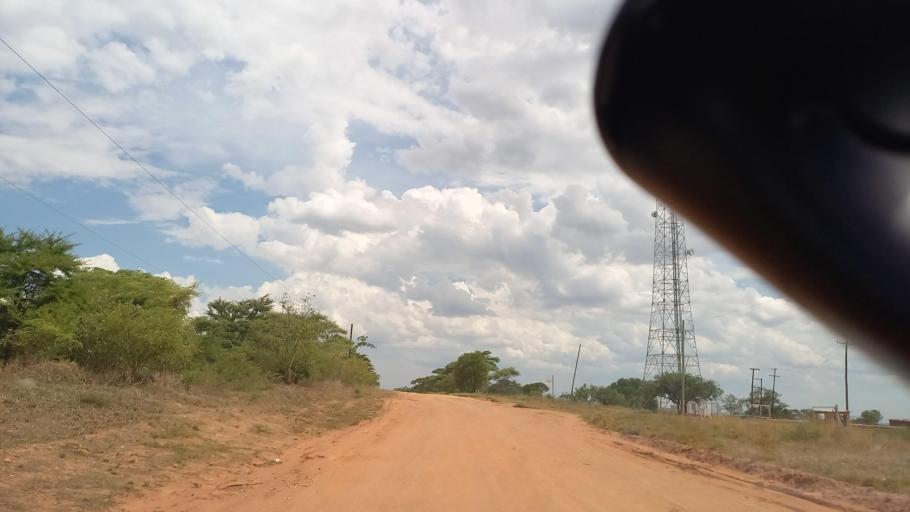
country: ZM
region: Southern
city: Nakambala
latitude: -16.0357
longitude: 27.9706
